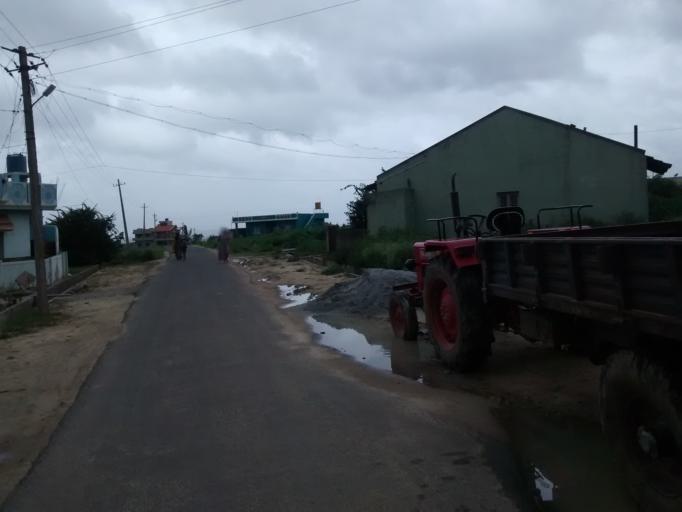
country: IN
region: Karnataka
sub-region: Hassan
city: Hassan
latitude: 12.9537
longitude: 76.1304
